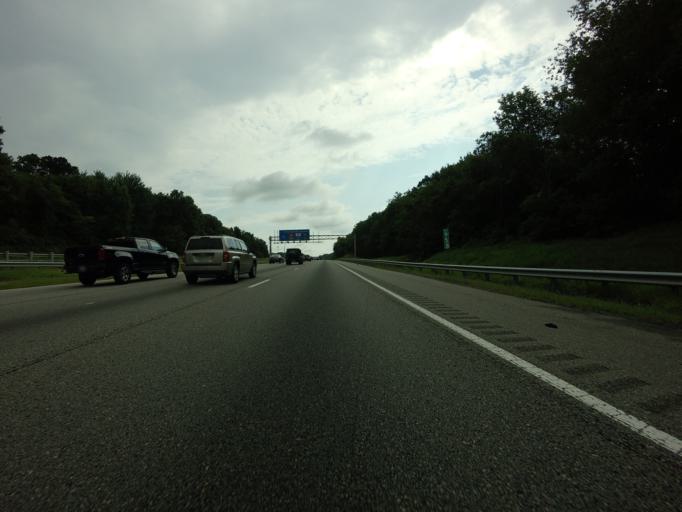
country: US
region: Maryland
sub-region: Cecil County
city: Charlestown
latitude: 39.6077
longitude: -76.0206
